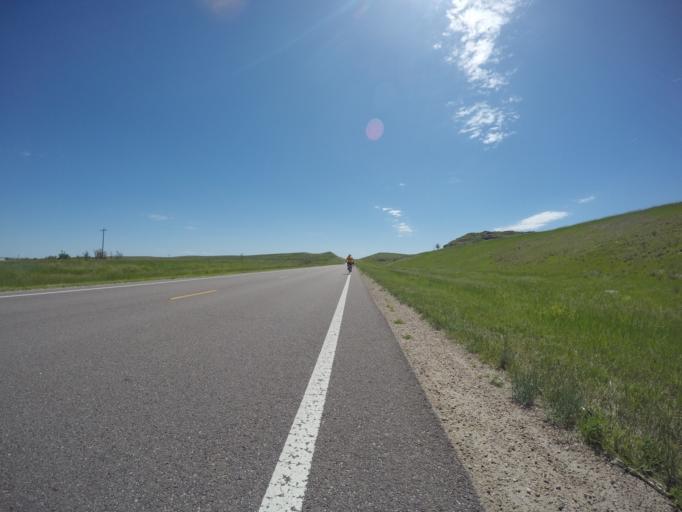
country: US
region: Kansas
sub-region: Rawlins County
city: Atwood
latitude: 39.8134
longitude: -101.0057
